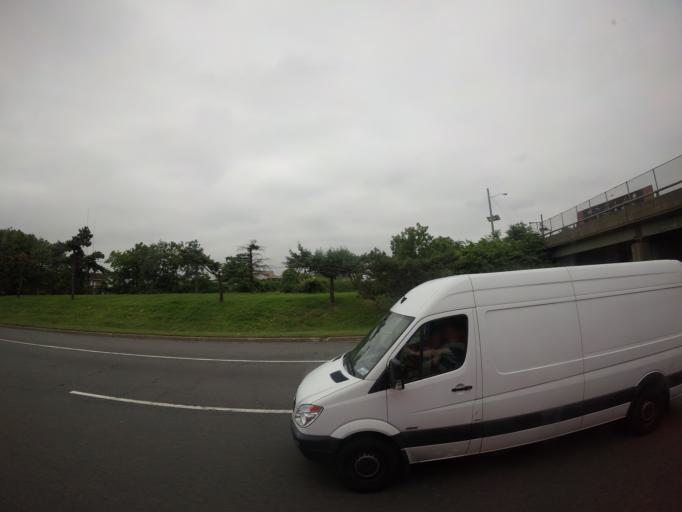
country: US
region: New Jersey
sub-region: Hudson County
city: Secaucus
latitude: 40.7747
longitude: -74.0597
